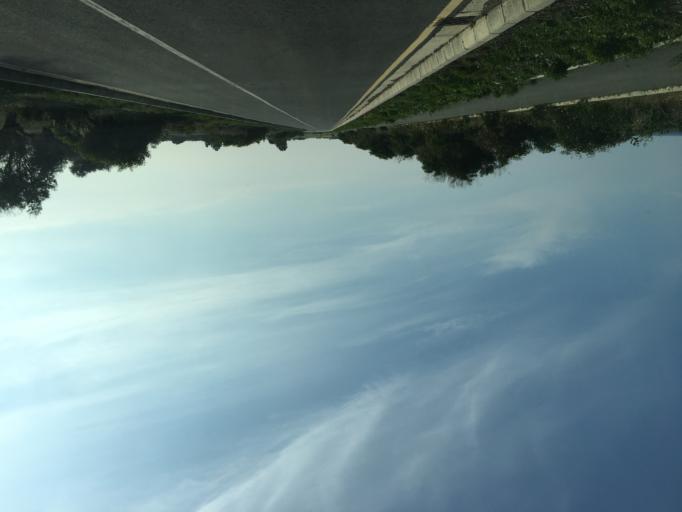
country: CY
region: Larnaka
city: Tersefanou
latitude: 34.7988
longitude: 33.5167
